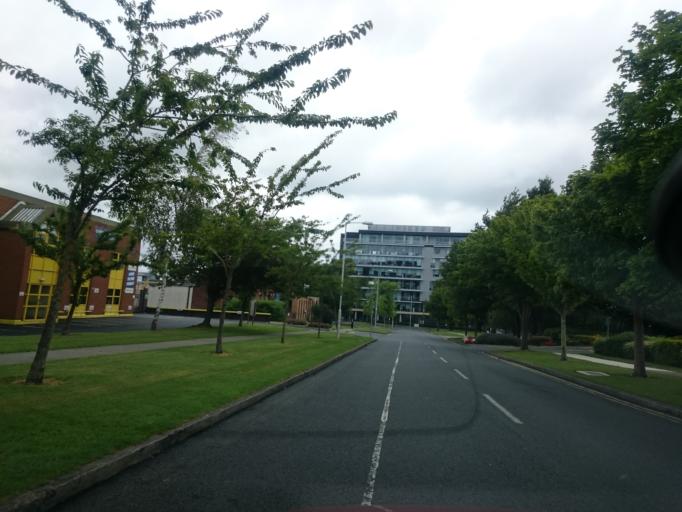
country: IE
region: Leinster
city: Sandyford
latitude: 53.2756
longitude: -6.2117
